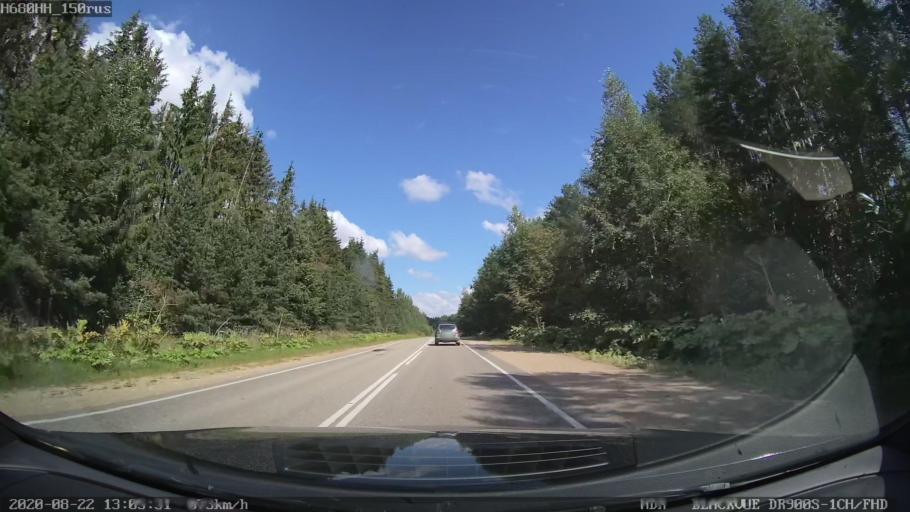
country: RU
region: Tverskaya
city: Bezhetsk
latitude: 57.6729
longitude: 36.4482
